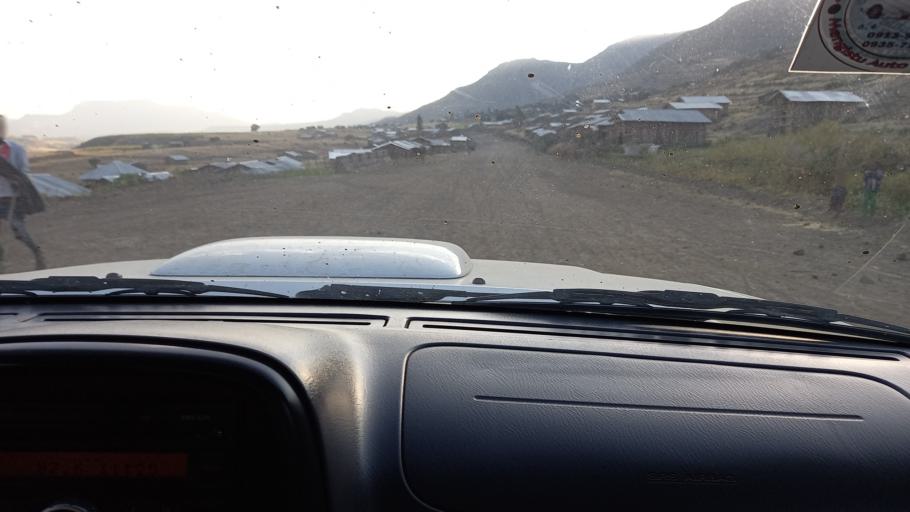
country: ET
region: Amhara
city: Debark'
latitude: 13.1165
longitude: 38.0248
